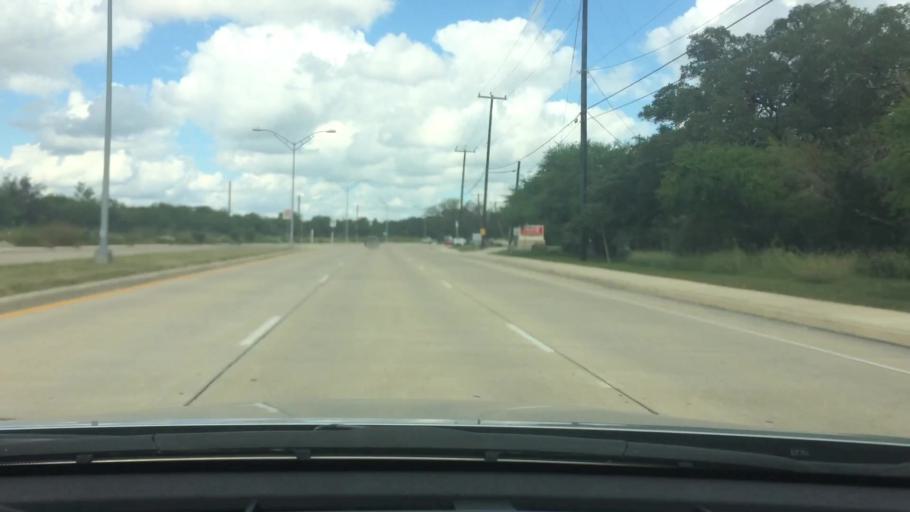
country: US
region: Texas
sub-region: Bexar County
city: Hollywood Park
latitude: 29.6247
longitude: -98.4236
